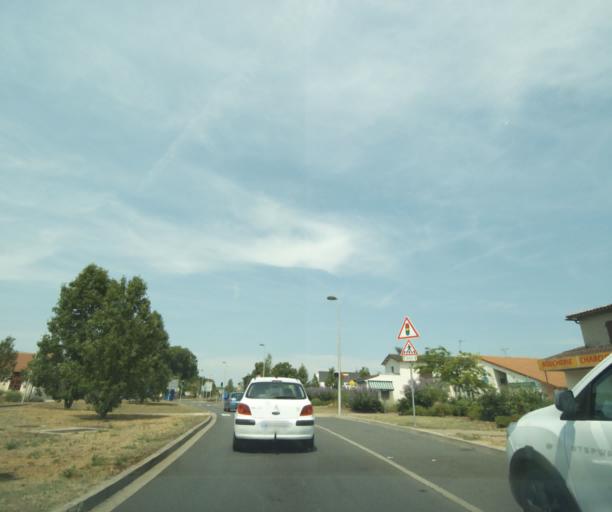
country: FR
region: Poitou-Charentes
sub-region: Departement de la Vienne
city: Antran
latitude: 46.8763
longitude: 0.5653
